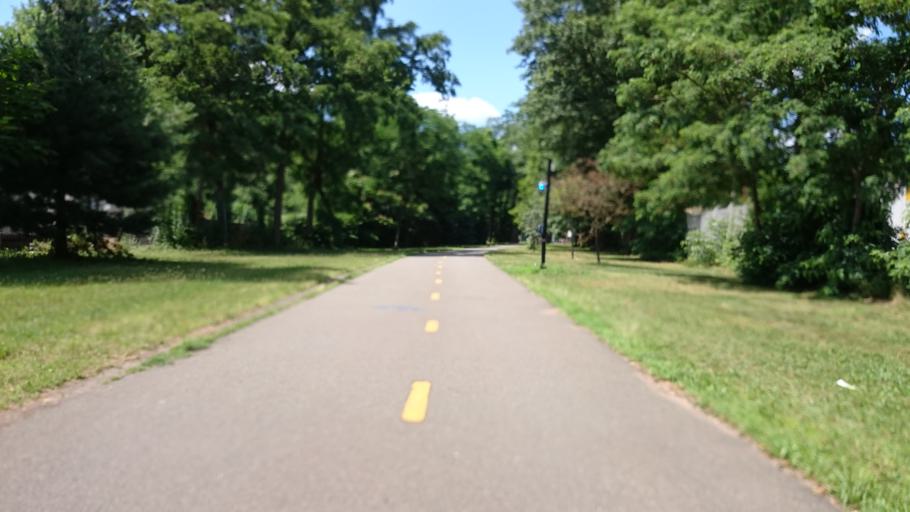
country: US
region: Connecticut
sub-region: New Haven County
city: New Haven
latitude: 41.3253
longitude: -72.9313
